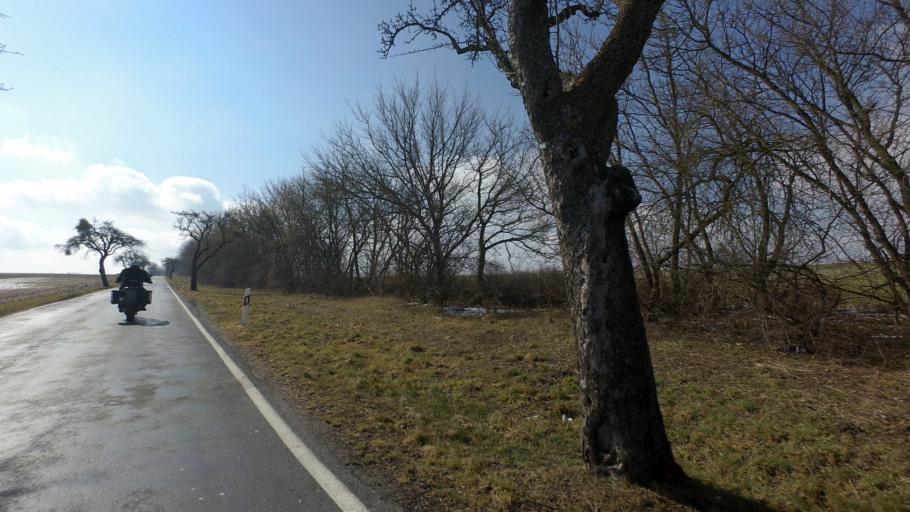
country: DE
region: Brandenburg
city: Werneuchen
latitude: 52.7038
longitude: 13.7195
